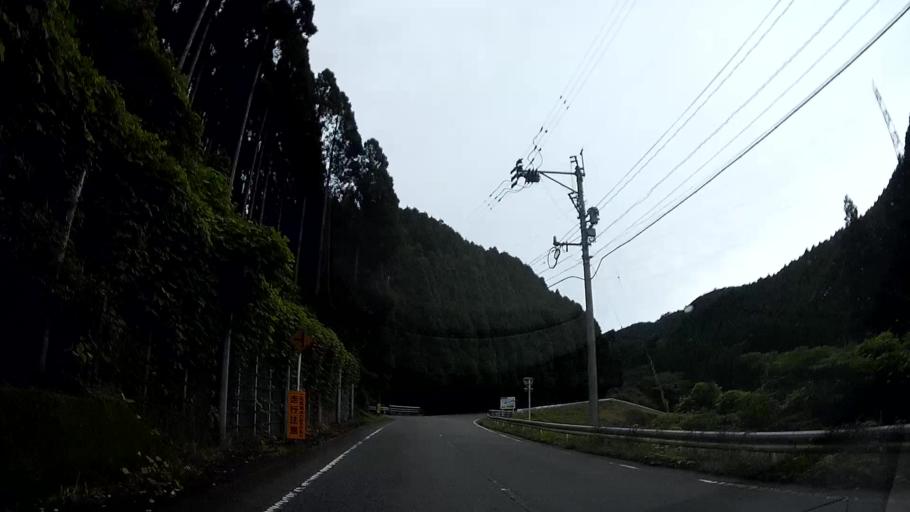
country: JP
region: Kumamoto
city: Kikuchi
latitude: 33.0375
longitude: 130.8913
